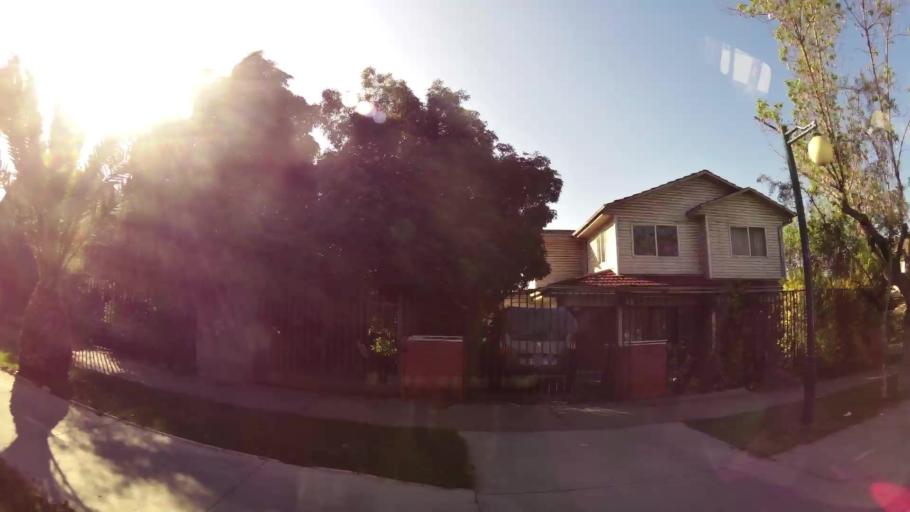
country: CL
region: Santiago Metropolitan
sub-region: Provincia de Santiago
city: Villa Presidente Frei, Nunoa, Santiago, Chile
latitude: -33.4395
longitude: -70.5833
